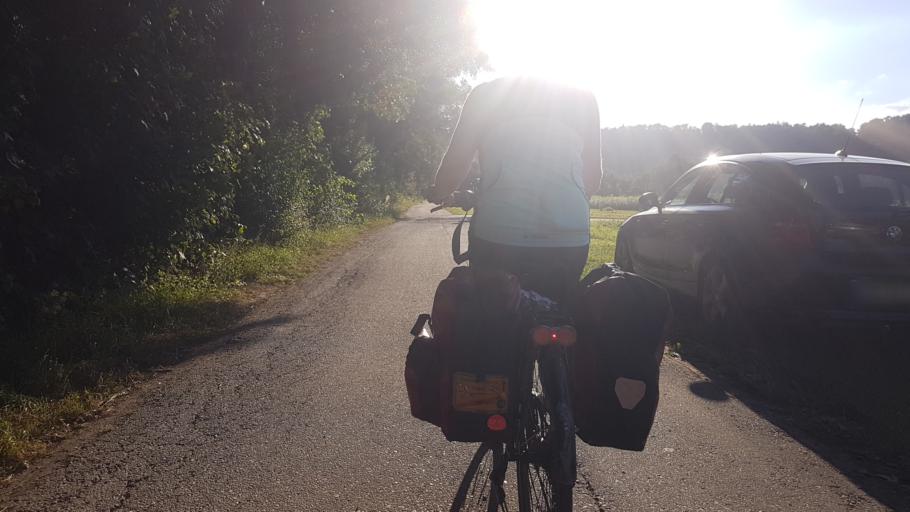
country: DE
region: Baden-Wuerttemberg
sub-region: Regierungsbezirk Stuttgart
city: Neudenau
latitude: 49.2889
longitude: 9.2665
